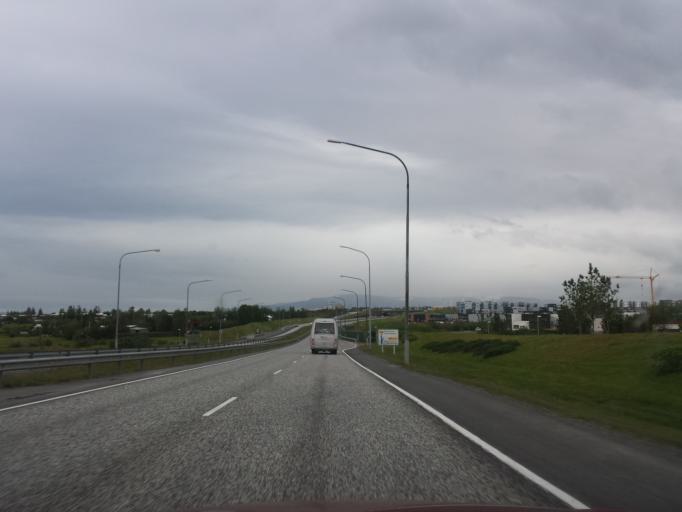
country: IS
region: Capital Region
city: Gardabaer
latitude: 64.0939
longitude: -21.9237
